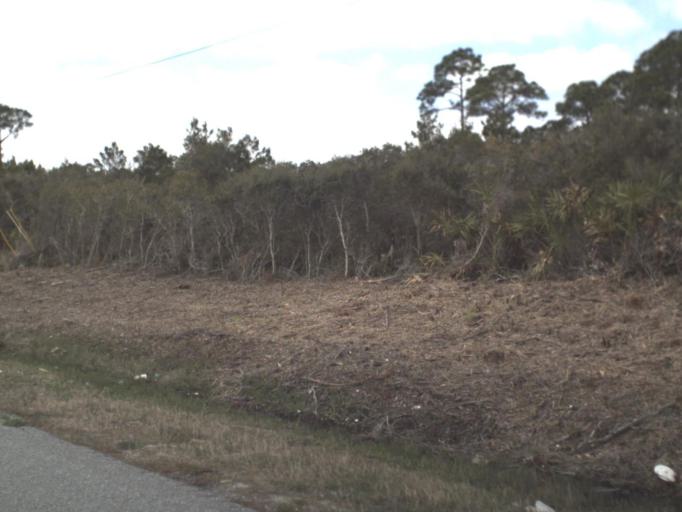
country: US
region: Florida
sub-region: Franklin County
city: Eastpoint
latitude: 29.7730
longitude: -84.7931
